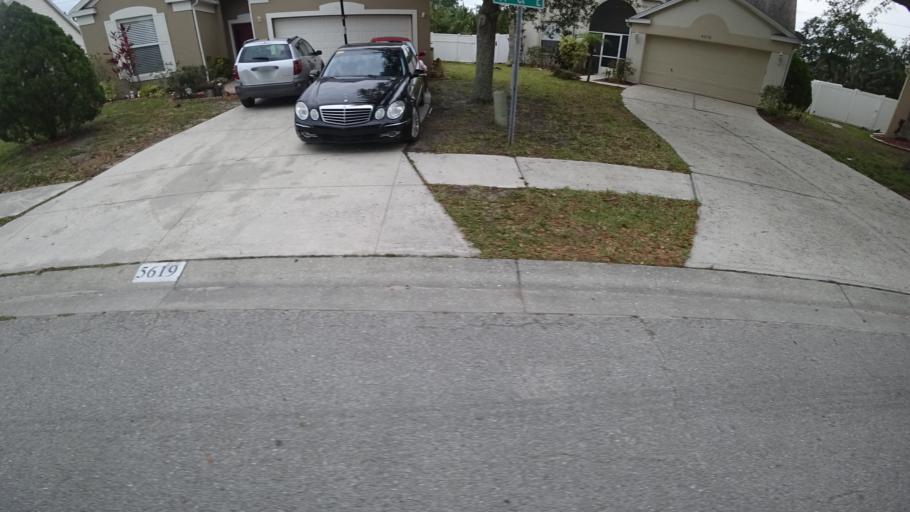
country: US
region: Florida
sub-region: Manatee County
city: Samoset
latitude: 27.4404
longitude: -82.5018
